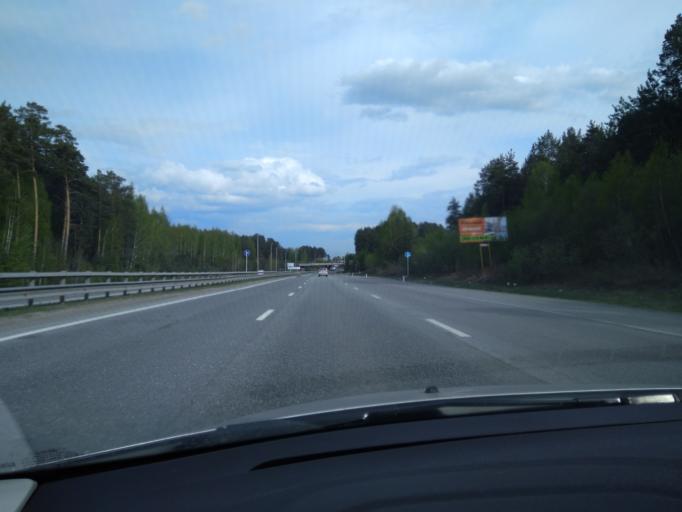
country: RU
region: Sverdlovsk
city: Shuvakish
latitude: 56.8894
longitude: 60.5446
